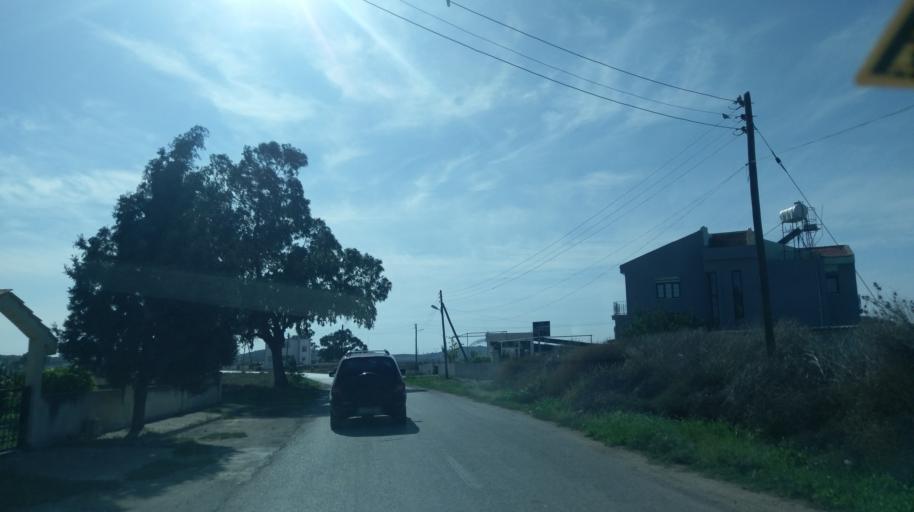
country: CY
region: Ammochostos
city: Trikomo
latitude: 35.3605
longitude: 33.9966
